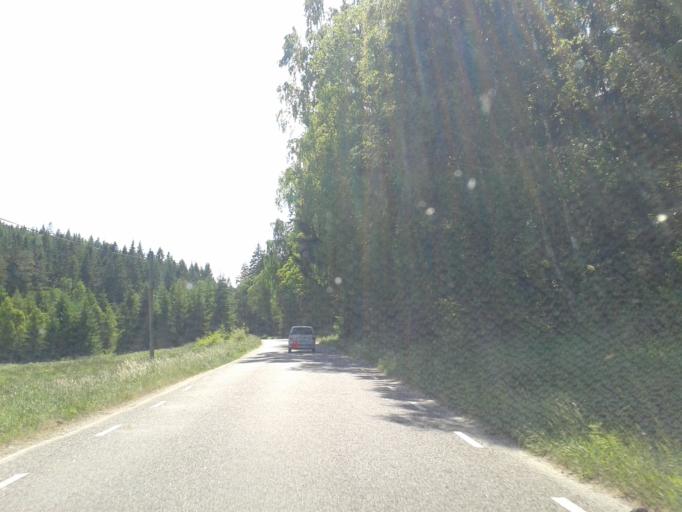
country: SE
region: Vaestra Goetaland
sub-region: Stenungsunds Kommun
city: Stora Hoga
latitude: 58.0094
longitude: 11.9223
